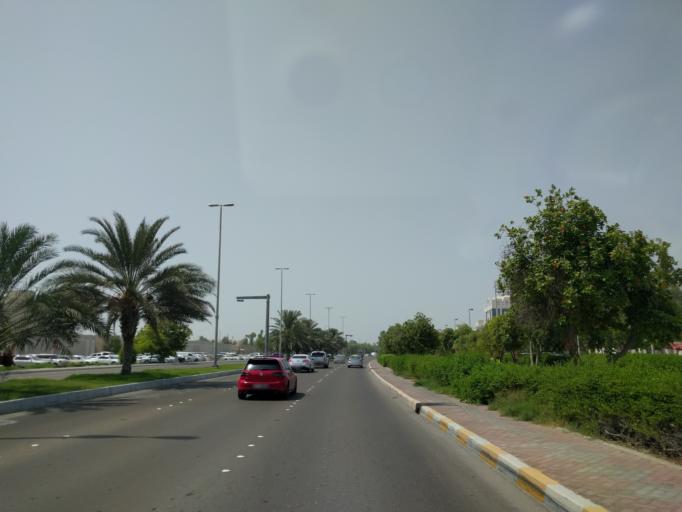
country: AE
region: Abu Dhabi
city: Abu Dhabi
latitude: 24.4311
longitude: 54.4297
